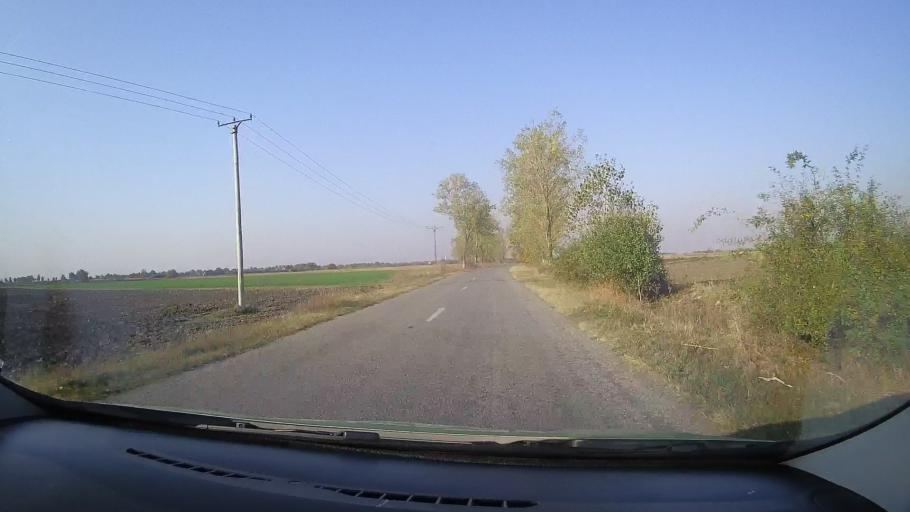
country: RO
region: Arad
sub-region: Comuna Graniceri
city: Siclau
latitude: 46.4981
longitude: 21.3833
